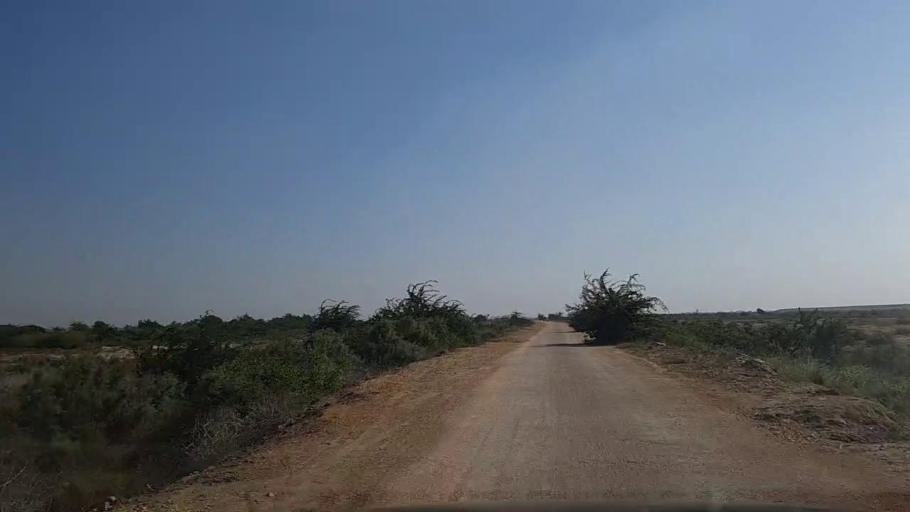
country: PK
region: Sindh
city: Daro Mehar
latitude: 24.8037
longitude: 68.0767
